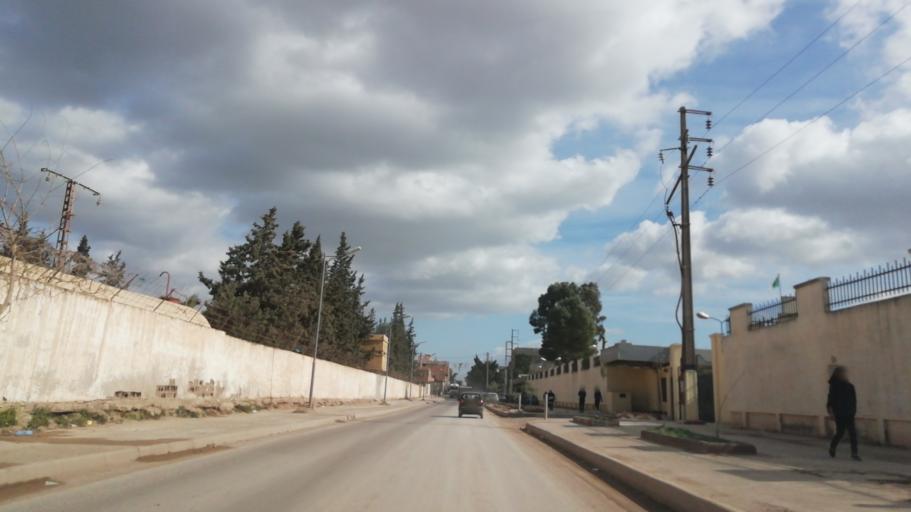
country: DZ
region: Oran
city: Sidi ech Chahmi
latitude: 35.6523
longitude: -0.5716
